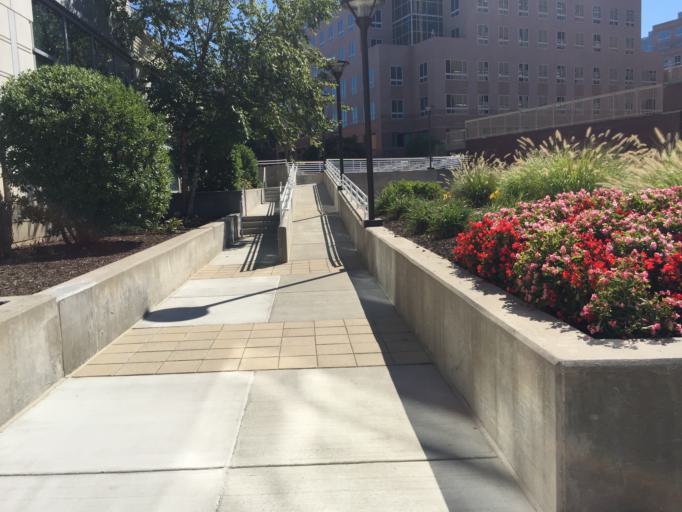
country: US
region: Virginia
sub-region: Arlington County
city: Arlington
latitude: 38.8857
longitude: -77.1024
